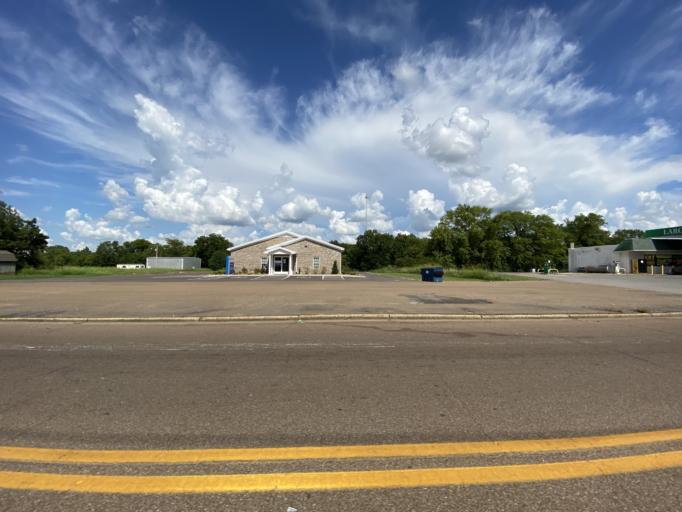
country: US
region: Tennessee
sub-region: Lauderdale County
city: Halls
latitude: 35.8719
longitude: -89.3963
